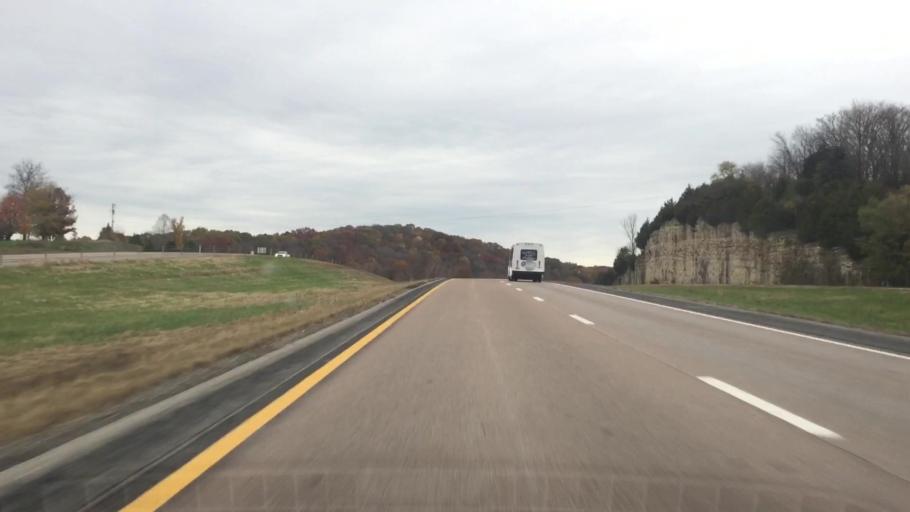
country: US
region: Missouri
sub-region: Cole County
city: Jefferson City
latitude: 38.6569
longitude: -92.2184
